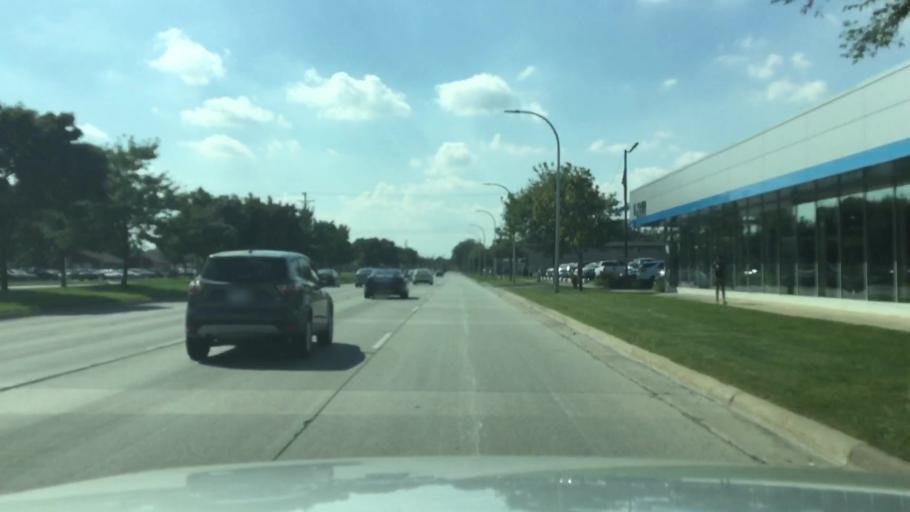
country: US
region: Michigan
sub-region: Wayne County
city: Wayne
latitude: 42.2829
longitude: -83.3667
